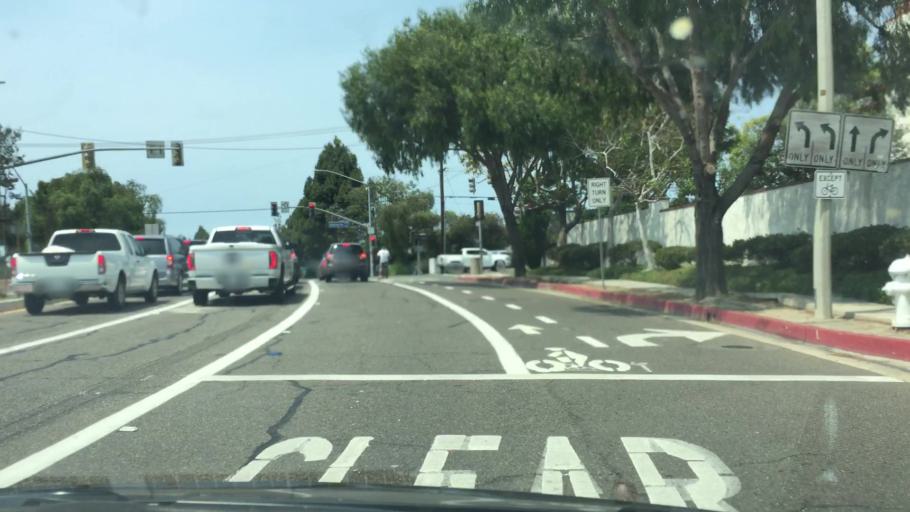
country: US
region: California
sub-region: Orange County
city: Costa Mesa
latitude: 33.6719
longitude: -117.9353
